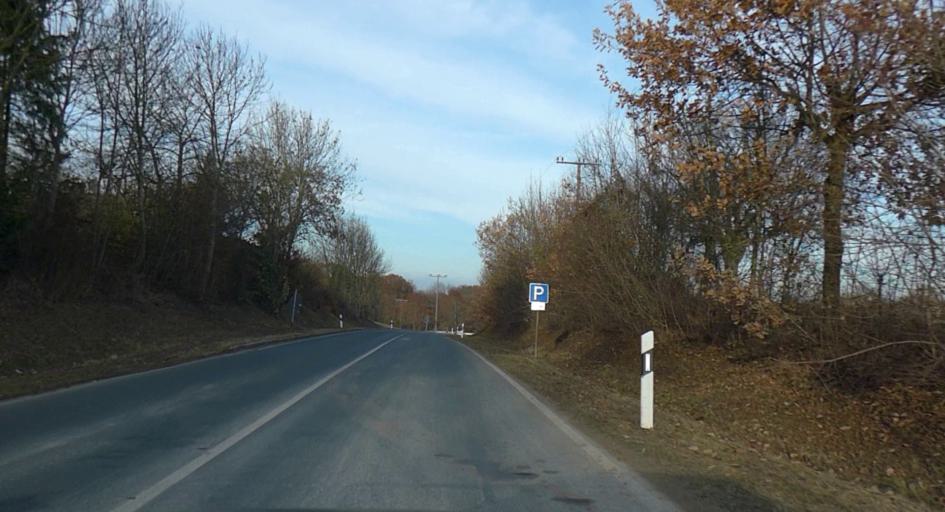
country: DE
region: Bavaria
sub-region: Regierungsbezirk Mittelfranken
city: Bubenreuth
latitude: 49.6169
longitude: 11.0285
